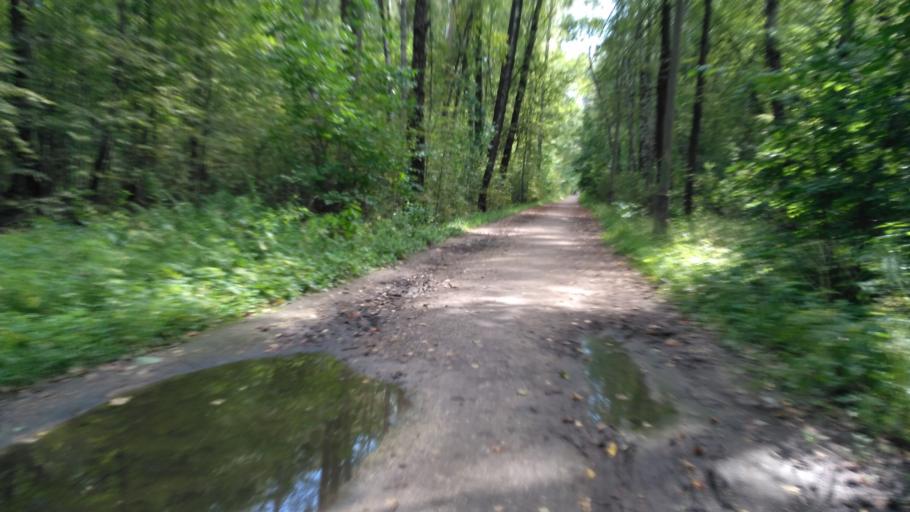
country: RU
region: Moscow
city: Ryazanskiy
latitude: 55.7692
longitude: 37.7595
